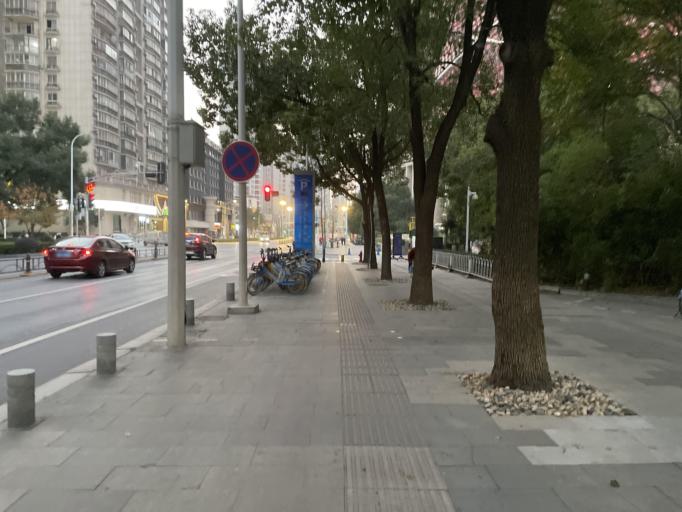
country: CN
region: Hubei
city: Jiang'an
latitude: 30.5532
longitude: 114.3434
